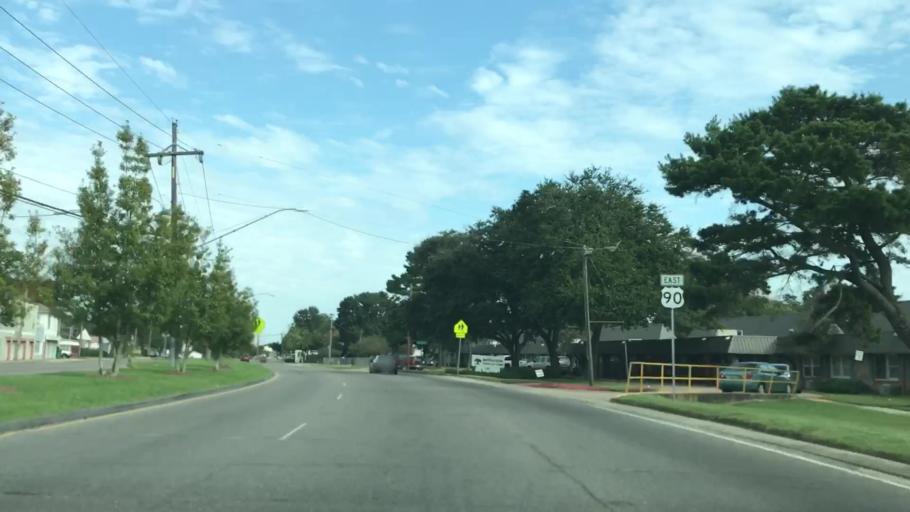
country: US
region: Louisiana
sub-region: Jefferson Parish
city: Jefferson
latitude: 29.9628
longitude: -90.1521
